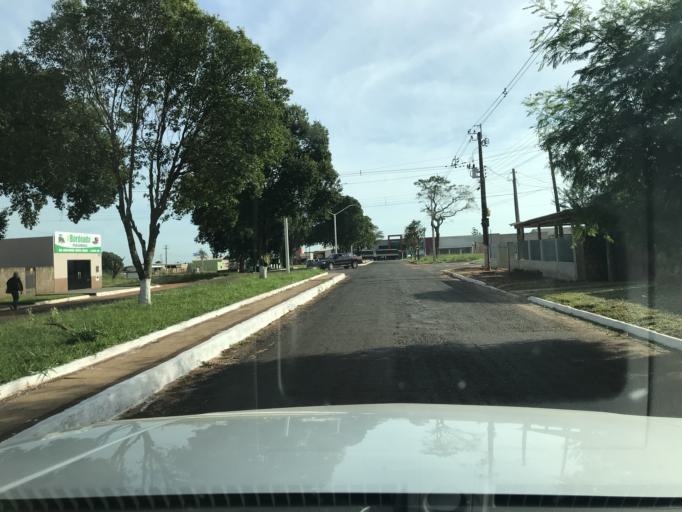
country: BR
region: Mato Grosso do Sul
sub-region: Iguatemi
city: Iguatemi
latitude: -23.6641
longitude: -54.5625
